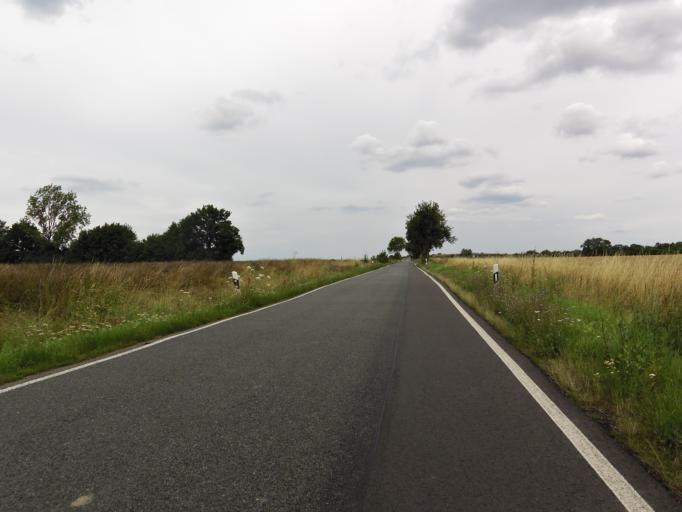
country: DE
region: Saxony
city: Rackwitz
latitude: 51.4128
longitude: 12.3777
